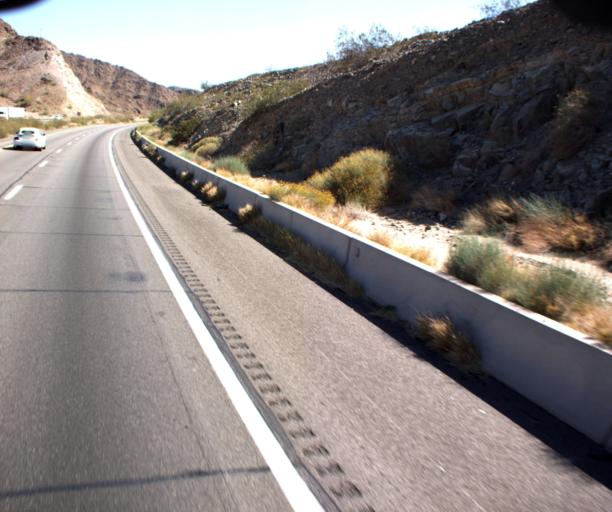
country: US
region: Arizona
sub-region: La Paz County
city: Ehrenberg
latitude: 33.6432
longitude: -114.3822
